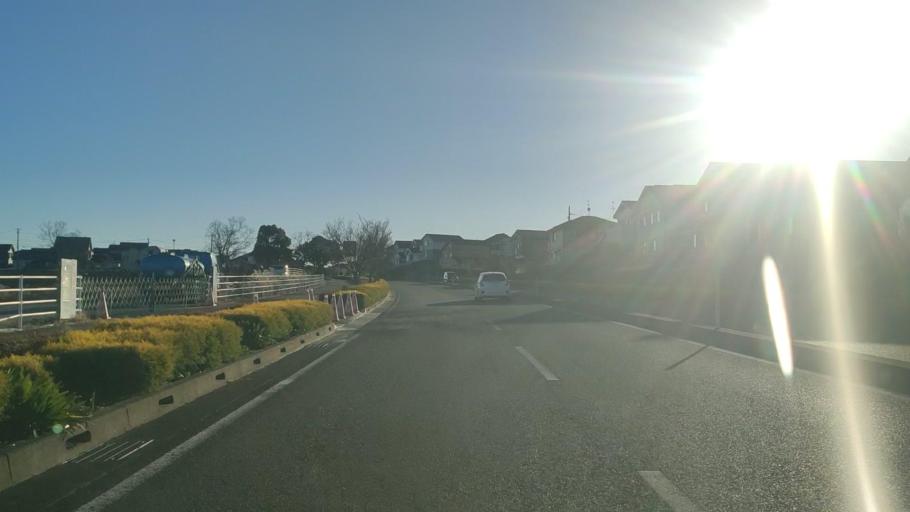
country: JP
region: Miyazaki
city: Miyazaki-shi
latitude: 31.8794
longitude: 131.3929
